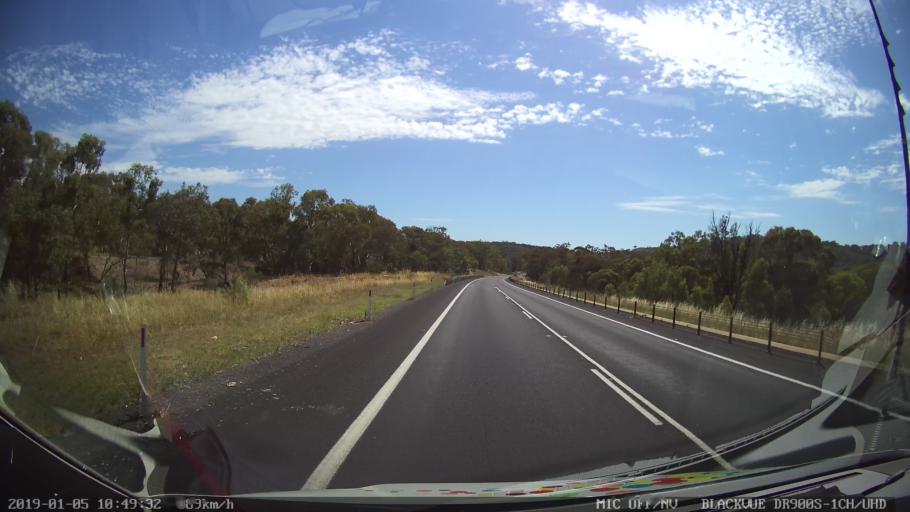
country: AU
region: New South Wales
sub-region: Warrumbungle Shire
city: Coonabarabran
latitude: -31.4335
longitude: 149.0623
